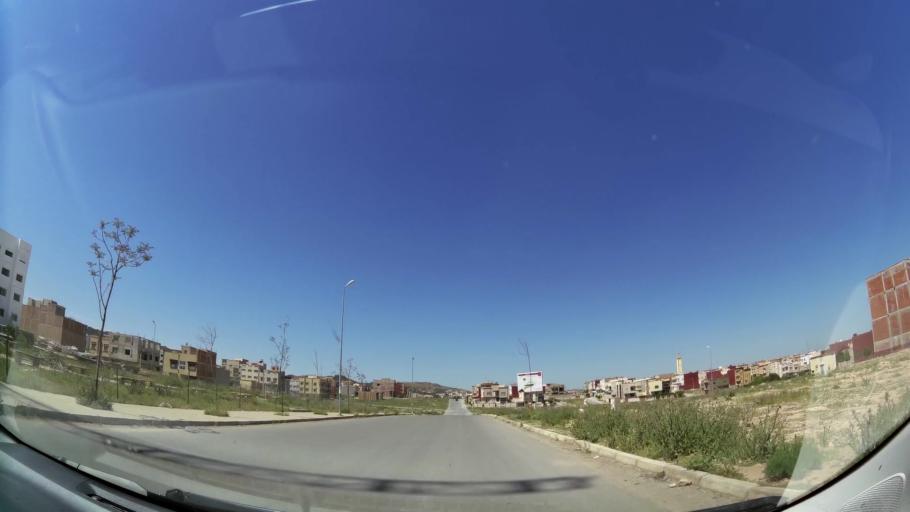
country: MA
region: Oriental
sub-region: Oujda-Angad
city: Oujda
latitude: 34.6549
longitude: -1.8820
